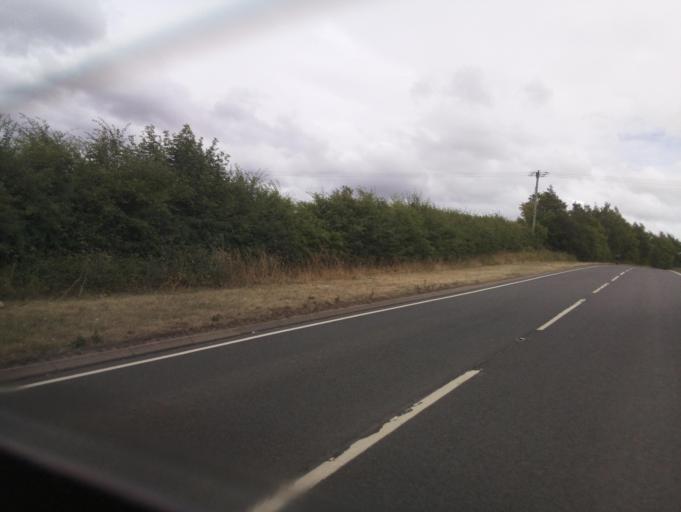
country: GB
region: England
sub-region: Leicestershire
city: Castle Donington
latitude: 52.8022
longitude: -1.3734
